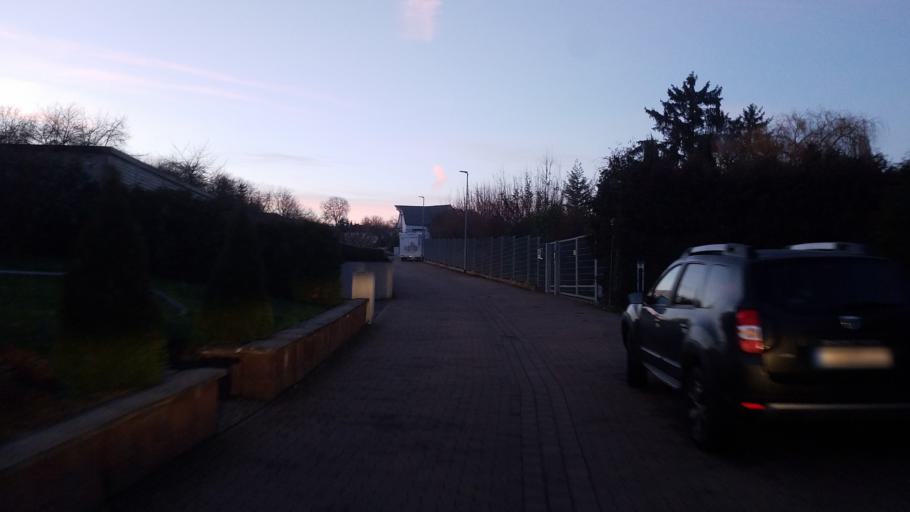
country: DE
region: Rheinland-Pfalz
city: Hargesheim
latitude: 49.8887
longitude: 7.8408
